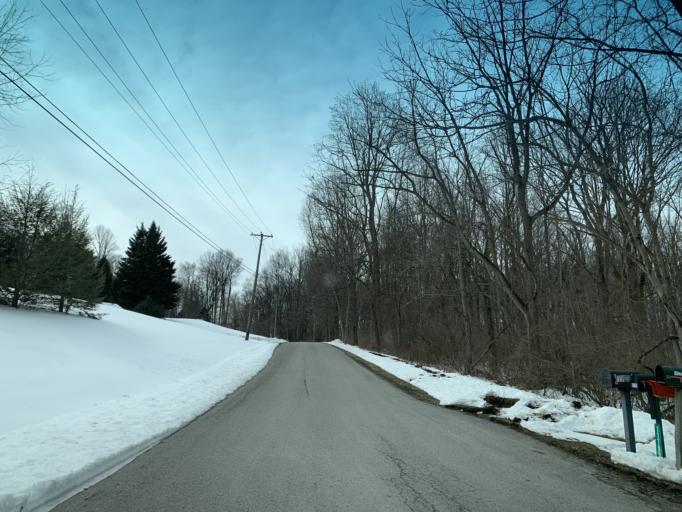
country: US
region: Pennsylvania
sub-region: York County
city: Red Lion
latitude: 39.8373
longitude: -76.6092
